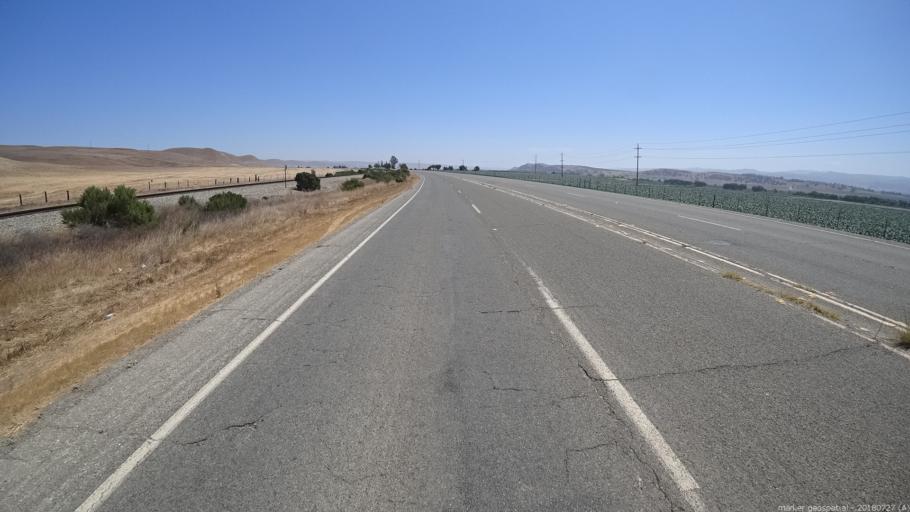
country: US
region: California
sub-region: Monterey County
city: King City
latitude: 36.1074
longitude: -120.9934
